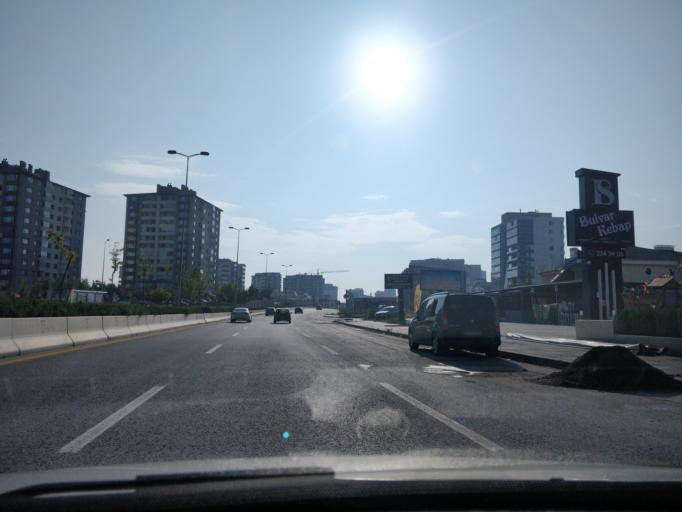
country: TR
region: Ankara
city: Etimesgut
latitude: 39.8974
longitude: 32.6389
